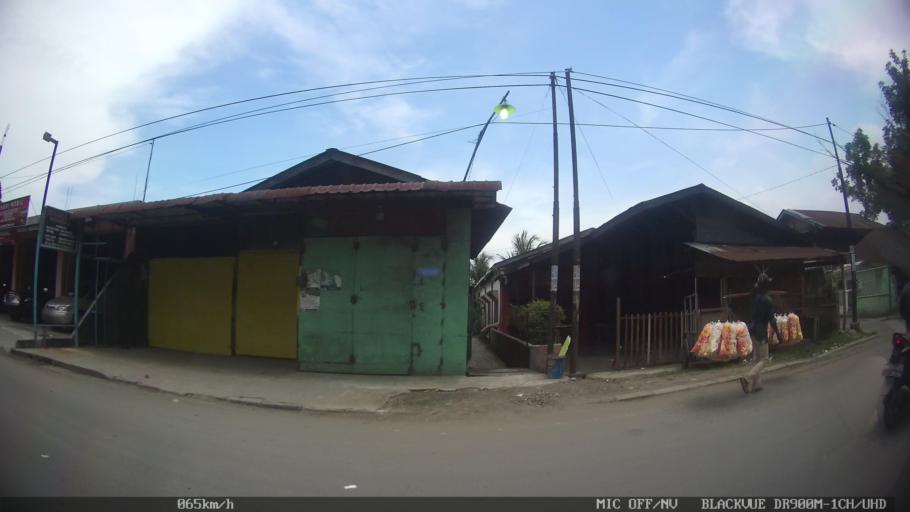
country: ID
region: North Sumatra
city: Labuhan Deli
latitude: 3.7038
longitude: 98.6785
